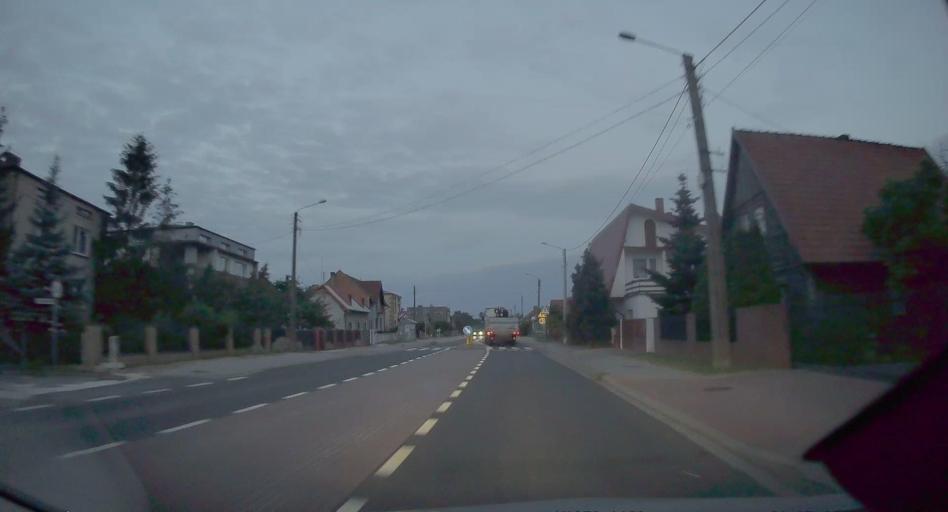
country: PL
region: Silesian Voivodeship
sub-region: Powiat klobucki
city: Opatow
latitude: 50.9274
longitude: 18.8649
